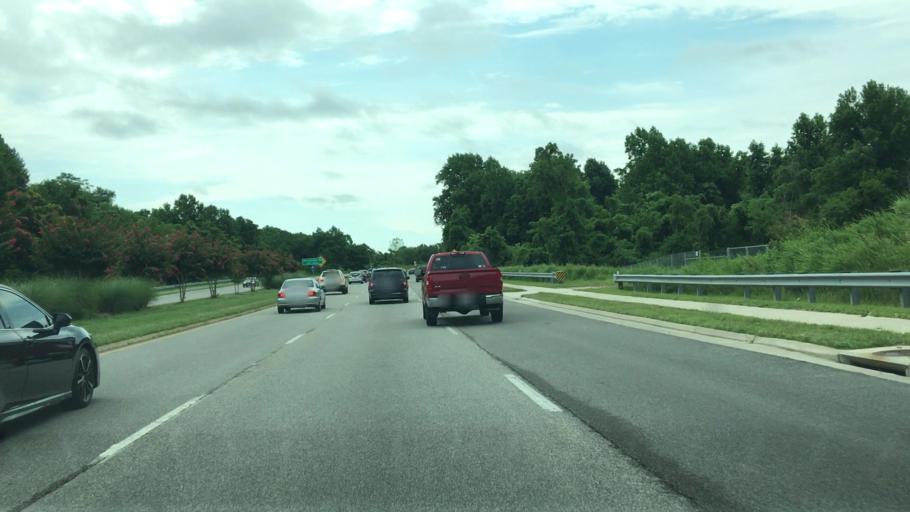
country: US
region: Virginia
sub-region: Prince William County
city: Dale City
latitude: 38.6559
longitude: -77.3195
